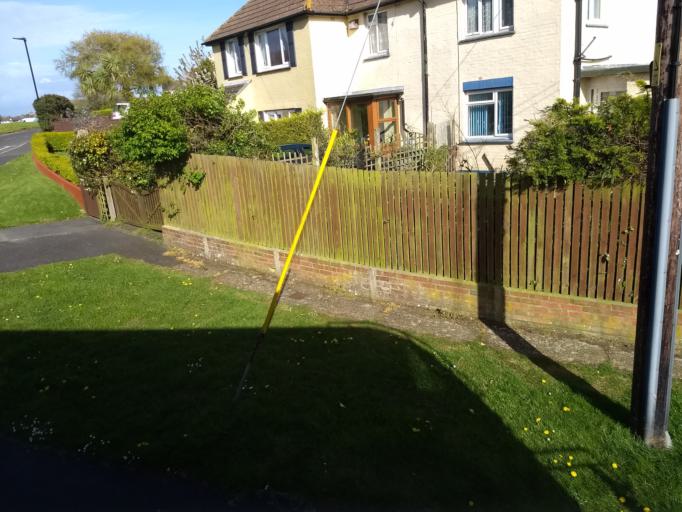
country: GB
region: England
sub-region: Isle of Wight
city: Seaview
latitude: 50.6965
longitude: -1.1134
